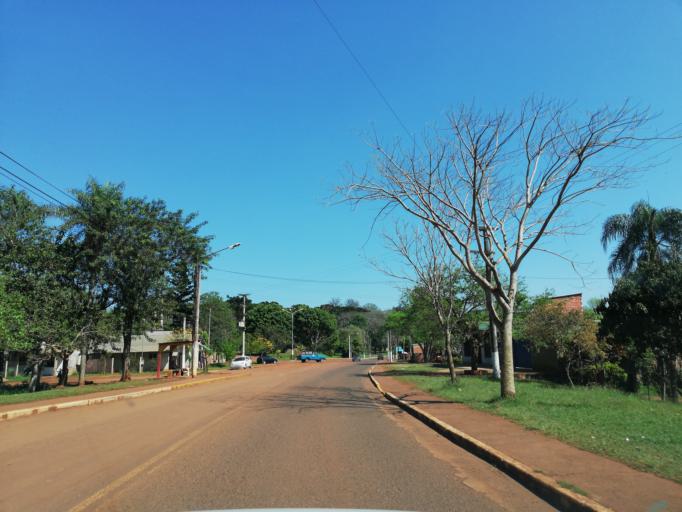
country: AR
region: Misiones
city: Puerto Eldorado
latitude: -26.4119
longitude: -54.6863
